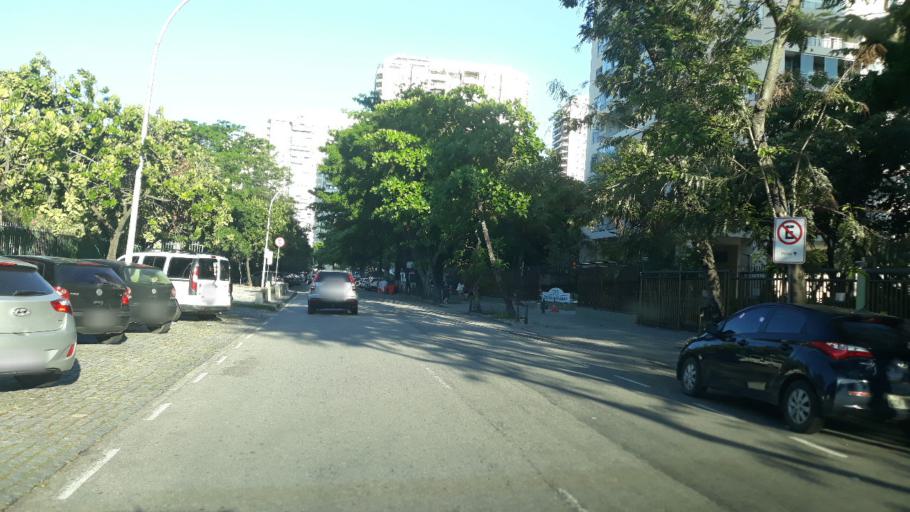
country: BR
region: Rio de Janeiro
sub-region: Rio De Janeiro
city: Rio de Janeiro
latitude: -23.0023
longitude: -43.3520
